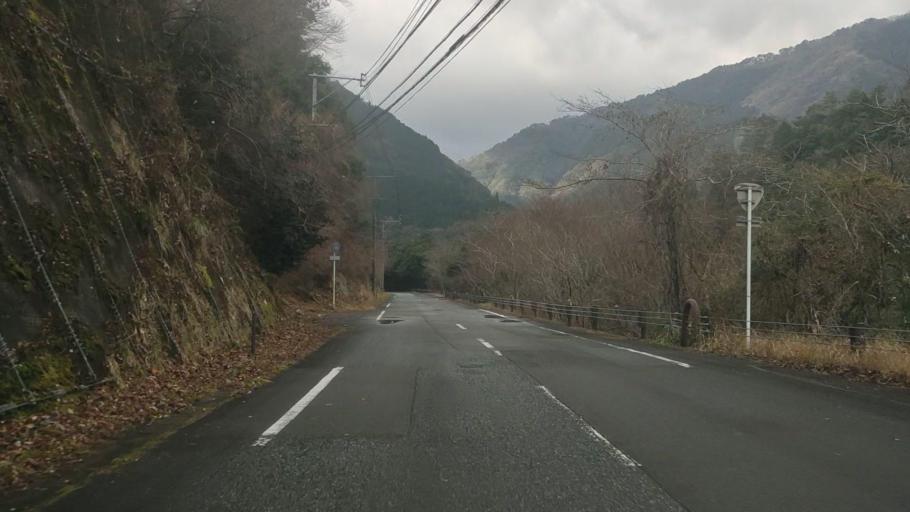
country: JP
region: Kumamoto
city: Matsubase
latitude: 32.5118
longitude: 130.9267
